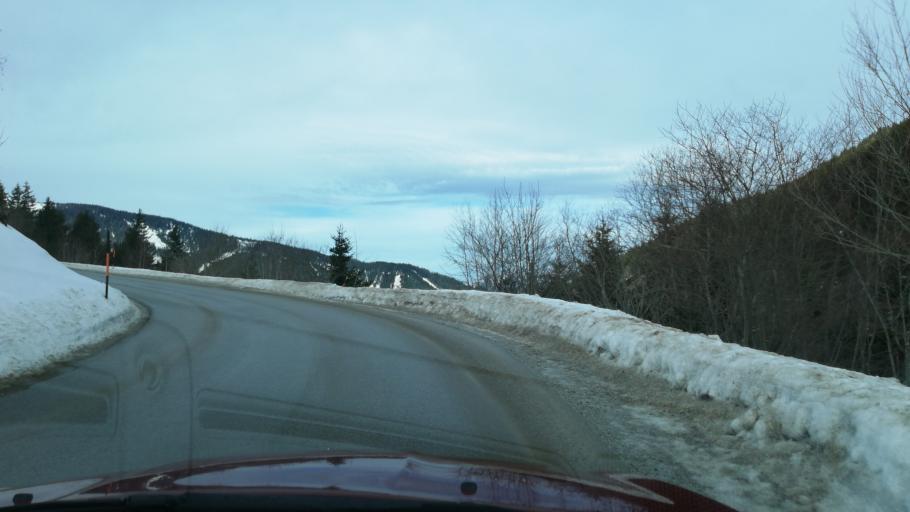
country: AT
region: Styria
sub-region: Politischer Bezirk Liezen
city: Donnersbach
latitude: 47.4324
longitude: 14.1594
